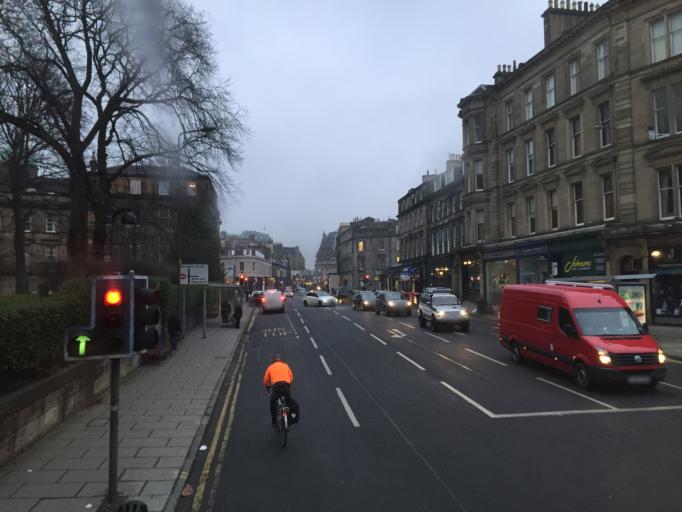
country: GB
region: Scotland
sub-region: Edinburgh
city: Edinburgh
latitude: 55.9518
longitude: -3.2122
